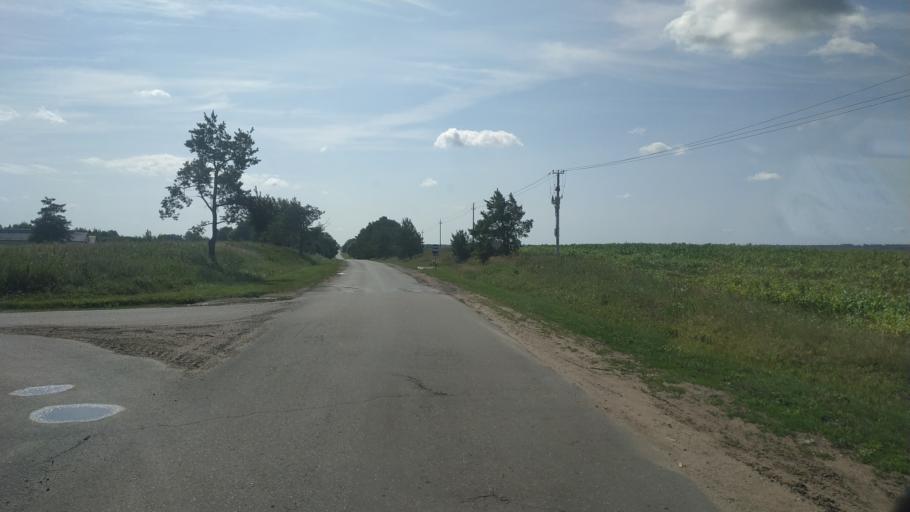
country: BY
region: Mogilev
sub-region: Mahilyowski Rayon
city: Veyno
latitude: 53.7844
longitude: 30.4358
